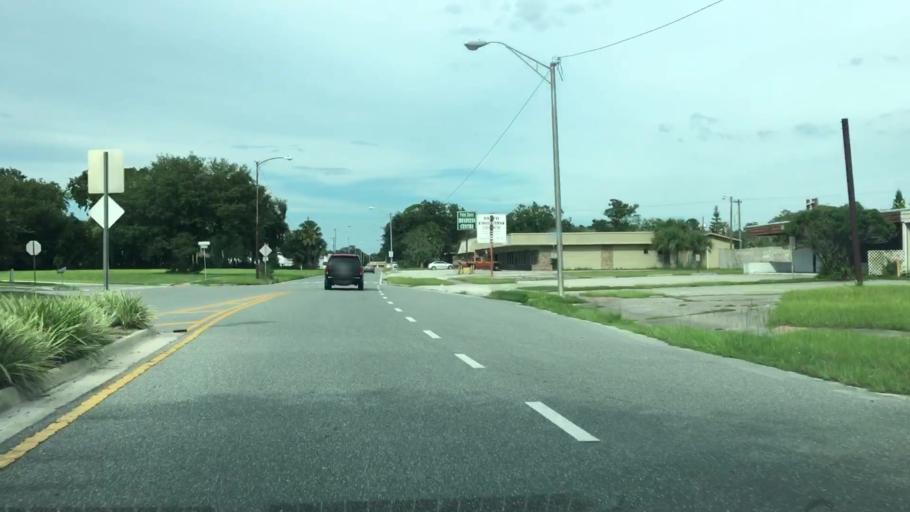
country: US
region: Florida
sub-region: Seminole County
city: Sanford
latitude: 28.7823
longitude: -81.2722
